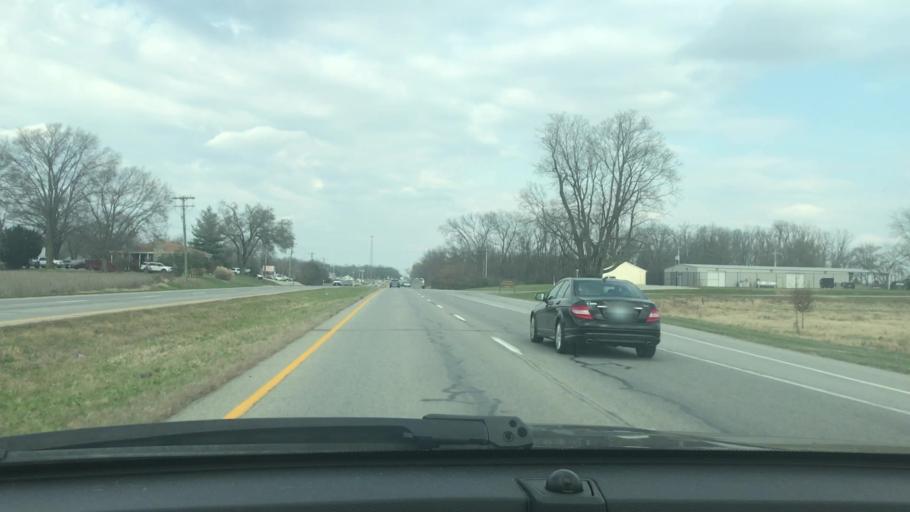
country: US
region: Indiana
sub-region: Clark County
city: Charlestown
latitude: 38.4065
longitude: -85.6751
